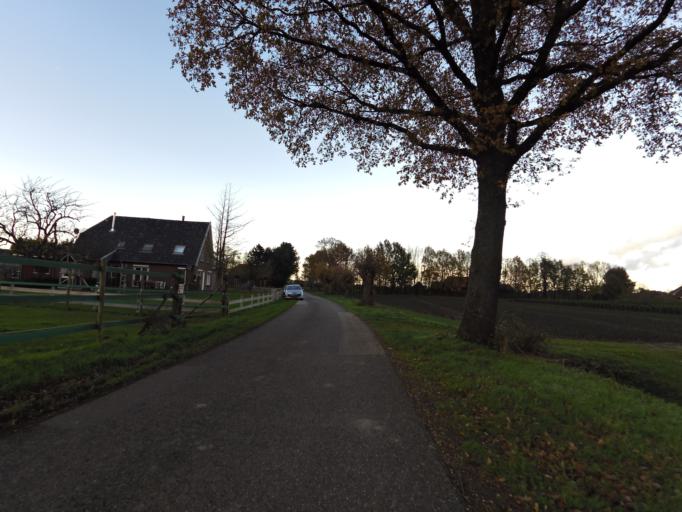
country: NL
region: Gelderland
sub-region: Oude IJsselstreek
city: Gendringen
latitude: 51.8433
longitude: 6.3840
